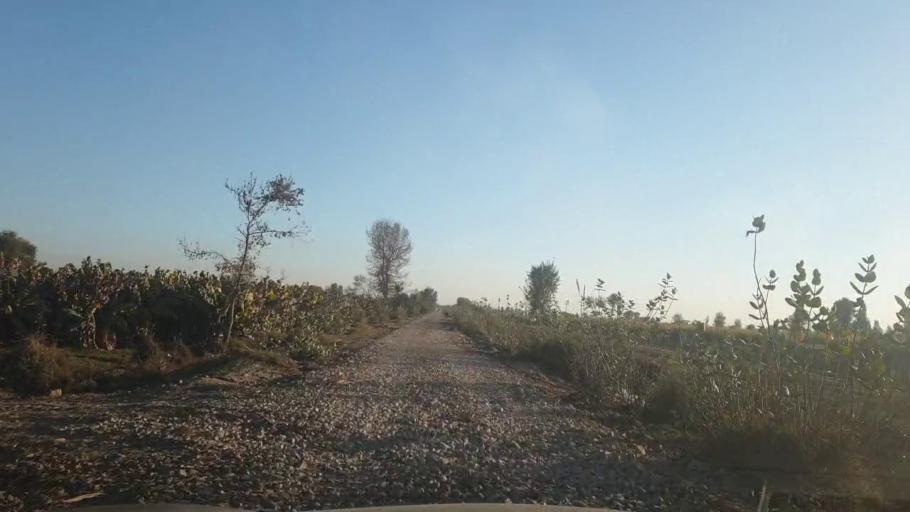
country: PK
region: Sindh
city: Ghotki
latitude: 28.0154
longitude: 69.2679
